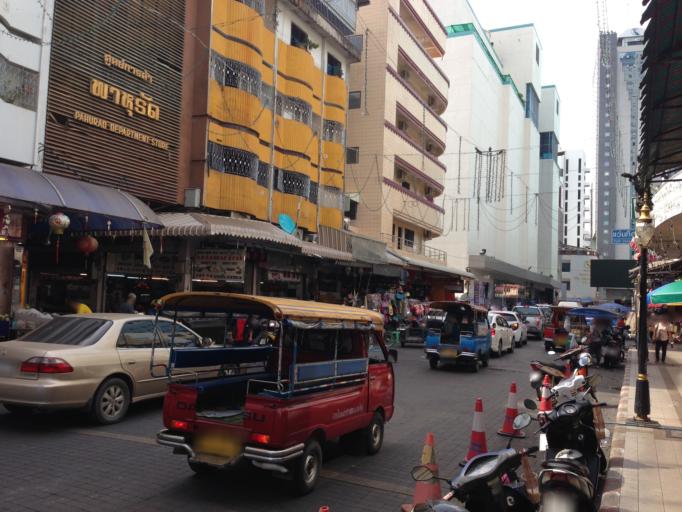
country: TH
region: Songkhla
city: Hat Yai
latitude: 7.0047
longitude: 100.4713
